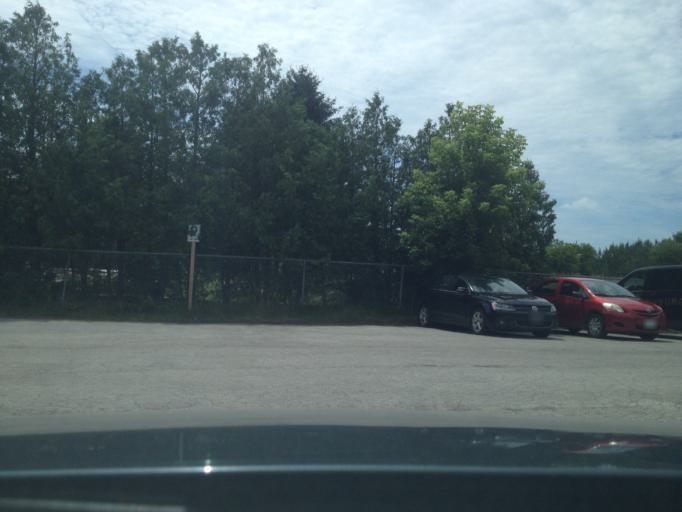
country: CA
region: Ontario
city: Norfolk County
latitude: 42.8536
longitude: -80.4019
